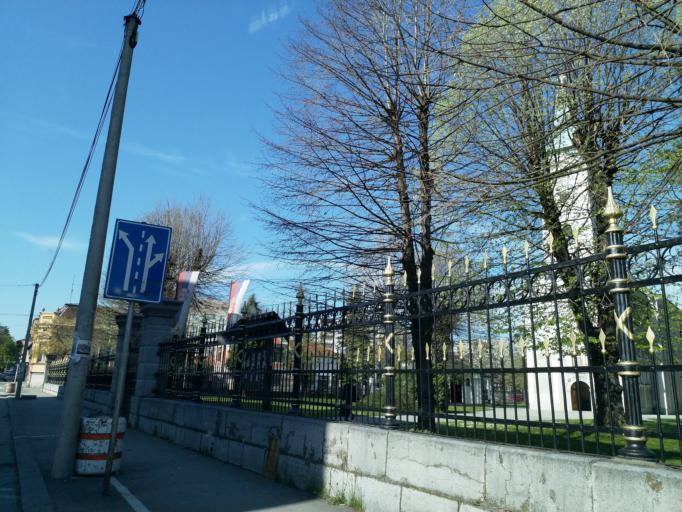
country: RS
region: Central Serbia
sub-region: Kolubarski Okrug
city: Valjevo
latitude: 44.2716
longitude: 19.8840
